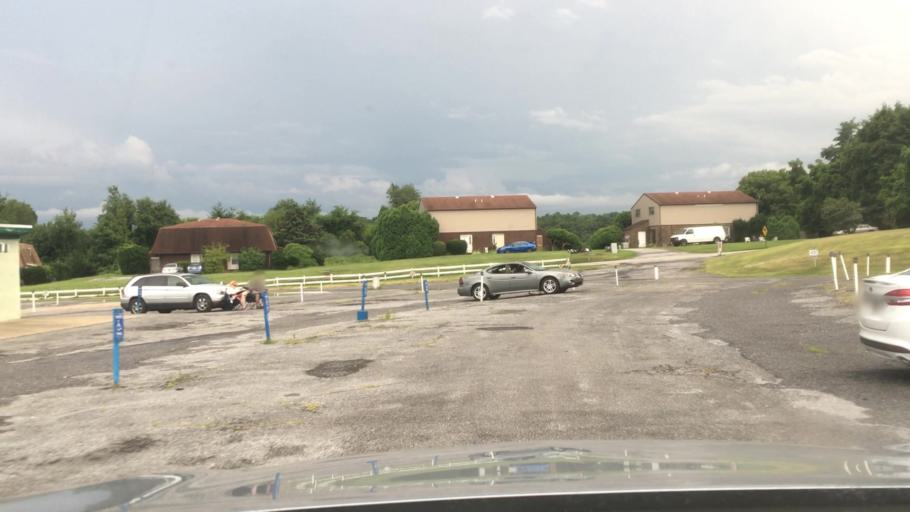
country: US
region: Pennsylvania
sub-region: York County
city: Dillsburg
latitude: 40.1255
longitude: -77.0204
